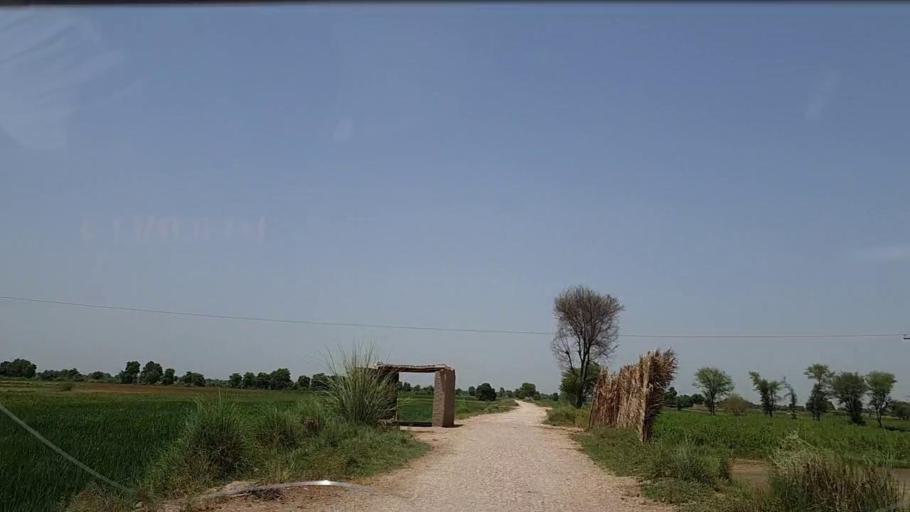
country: PK
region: Sindh
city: Tharu Shah
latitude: 26.9490
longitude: 68.0437
